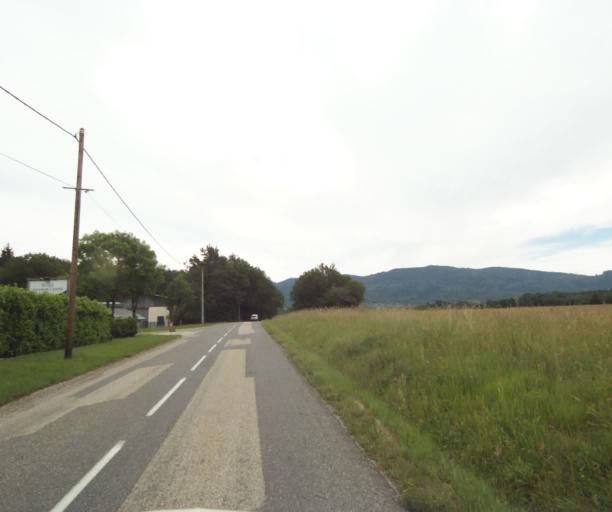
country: FR
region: Rhone-Alpes
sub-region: Departement de la Haute-Savoie
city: Perrignier
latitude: 46.3053
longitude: 6.4115
